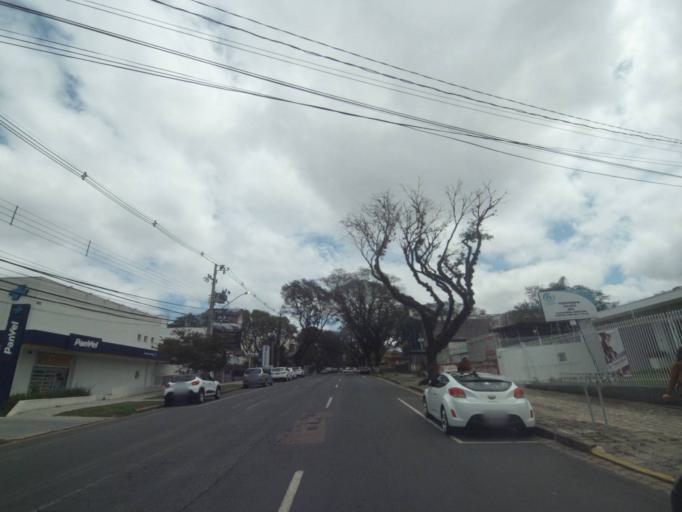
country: BR
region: Parana
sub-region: Curitiba
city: Curitiba
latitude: -25.4074
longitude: -49.2386
